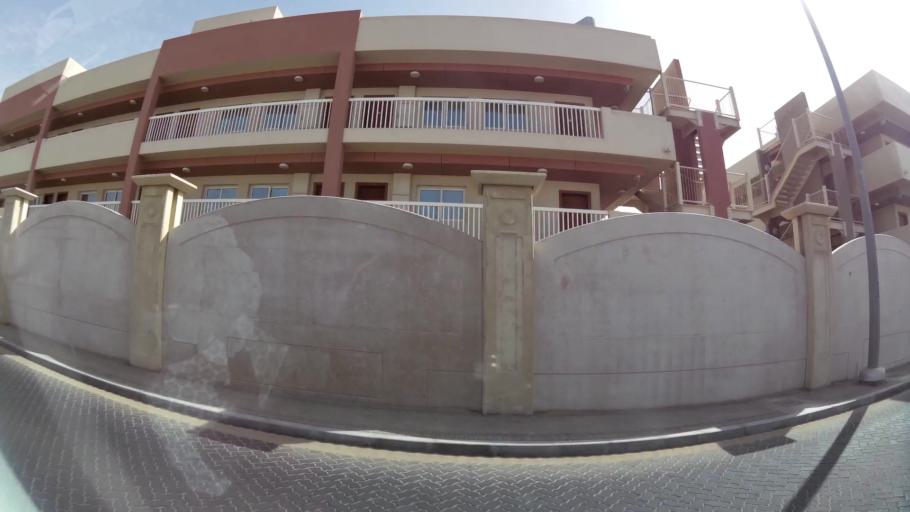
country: AE
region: Abu Dhabi
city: Abu Dhabi
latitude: 24.4131
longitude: 54.5462
